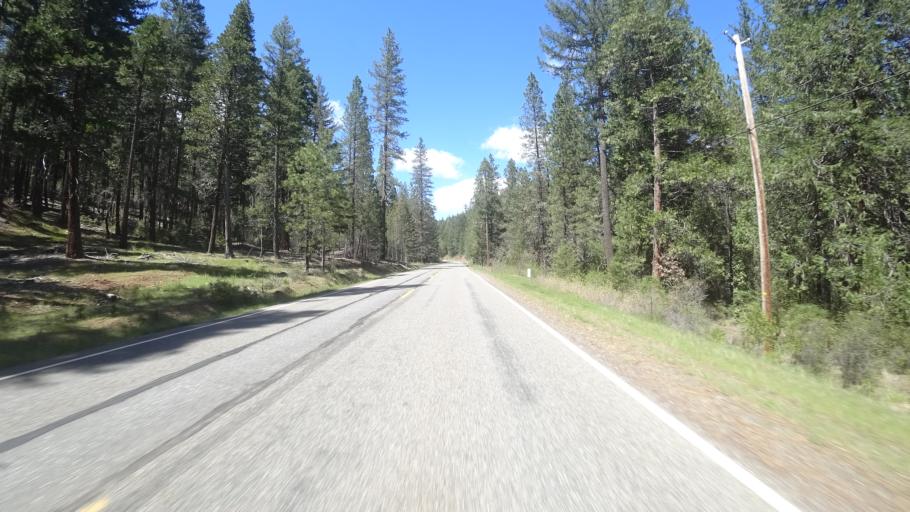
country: US
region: California
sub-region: Trinity County
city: Weaverville
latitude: 40.7595
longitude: -122.8873
